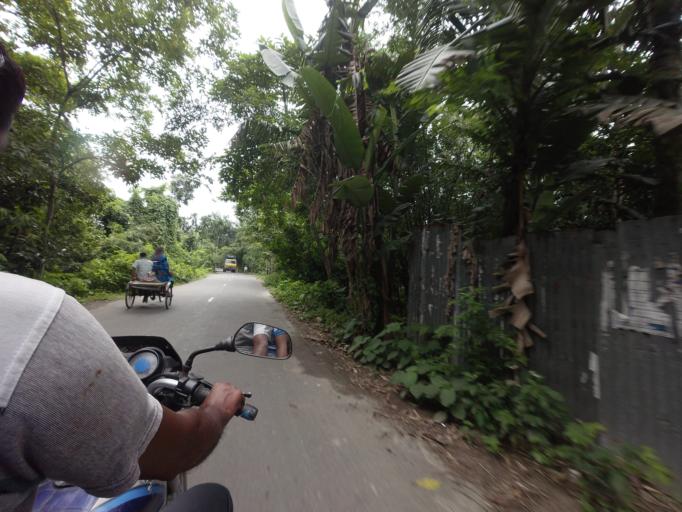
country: BD
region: Khulna
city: Kalia
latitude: 23.1587
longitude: 89.6439
